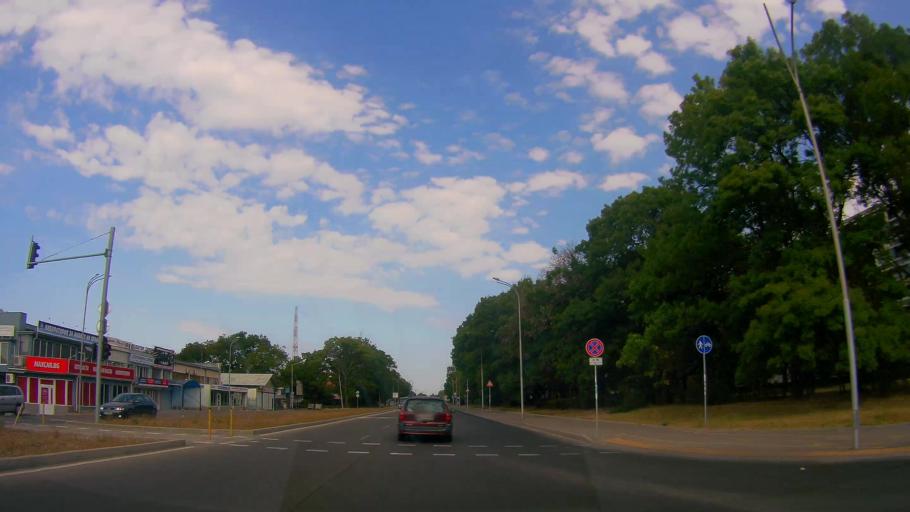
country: BG
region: Burgas
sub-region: Obshtina Burgas
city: Burgas
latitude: 42.5169
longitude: 27.4479
